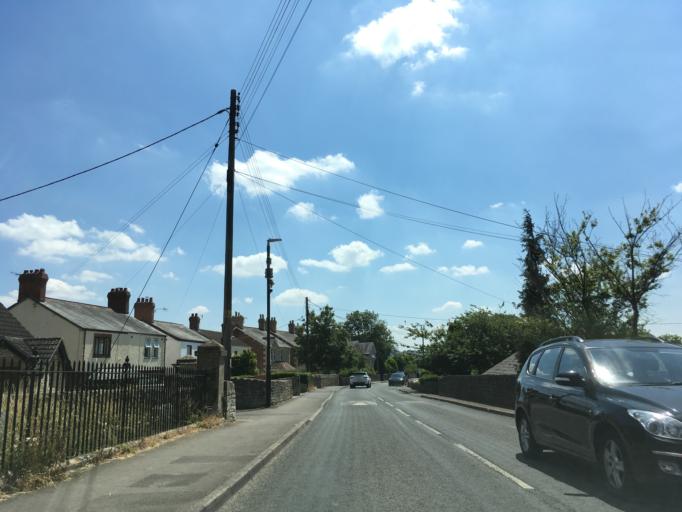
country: GB
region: England
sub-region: Gloucestershire
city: Stroud
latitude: 51.7596
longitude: -2.2324
